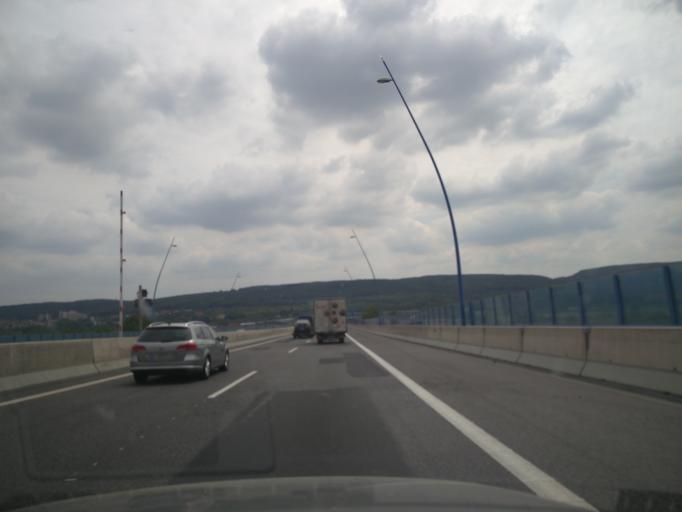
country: CZ
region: Praha
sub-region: Praha 12
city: Modrany
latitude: 49.9907
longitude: 14.3822
